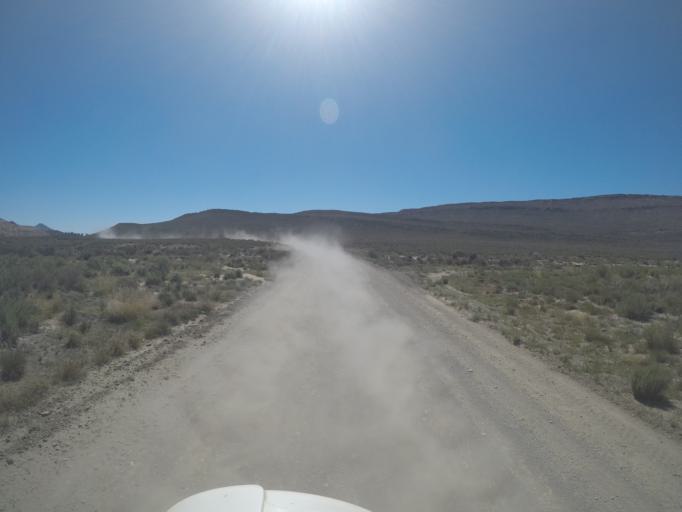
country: ZA
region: Western Cape
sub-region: Cape Winelands District Municipality
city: Ceres
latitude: -32.8283
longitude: 19.4544
